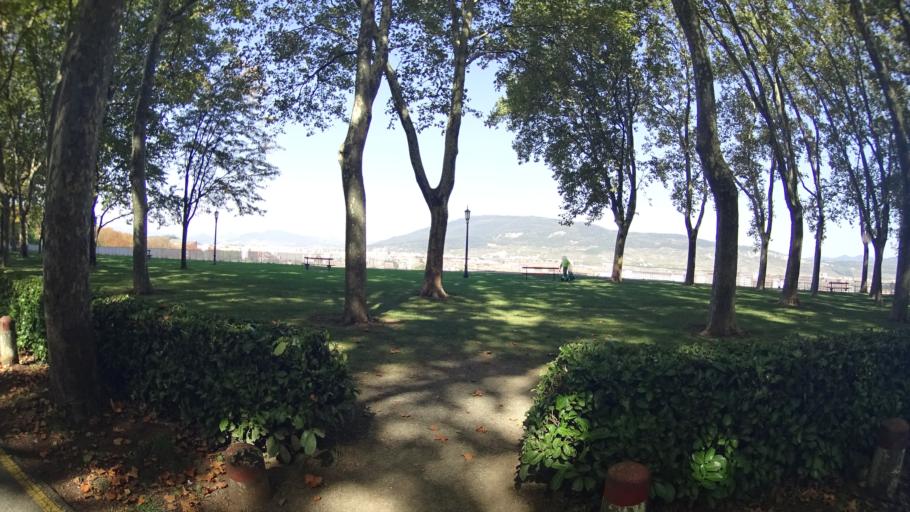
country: ES
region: Navarre
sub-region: Provincia de Navarra
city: Primer Ensanche
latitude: 42.8188
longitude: -1.6533
